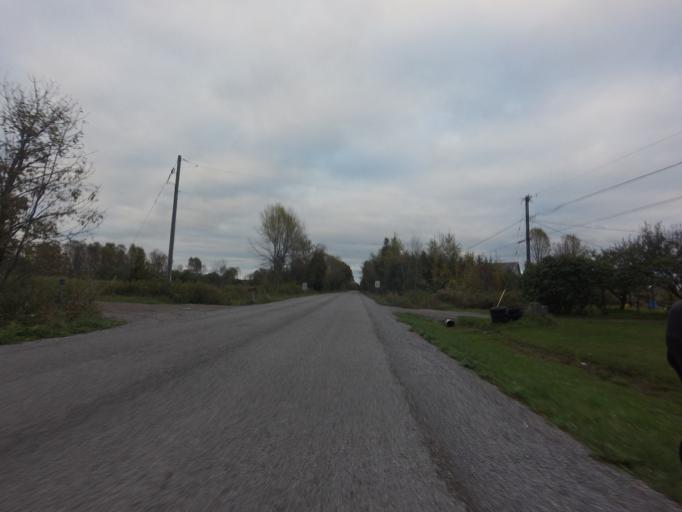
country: CA
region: Ontario
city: Quinte West
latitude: 44.0109
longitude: -77.7663
